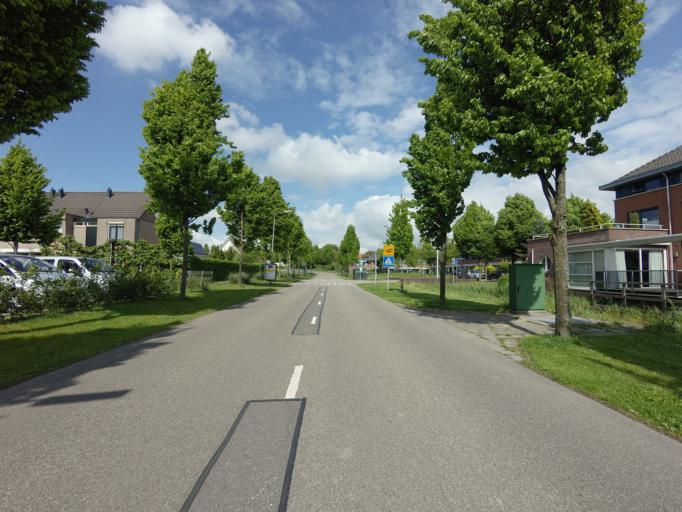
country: NL
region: South Holland
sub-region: Gemeente Zwijndrecht
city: Heerjansdam
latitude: 51.8324
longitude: 4.5624
